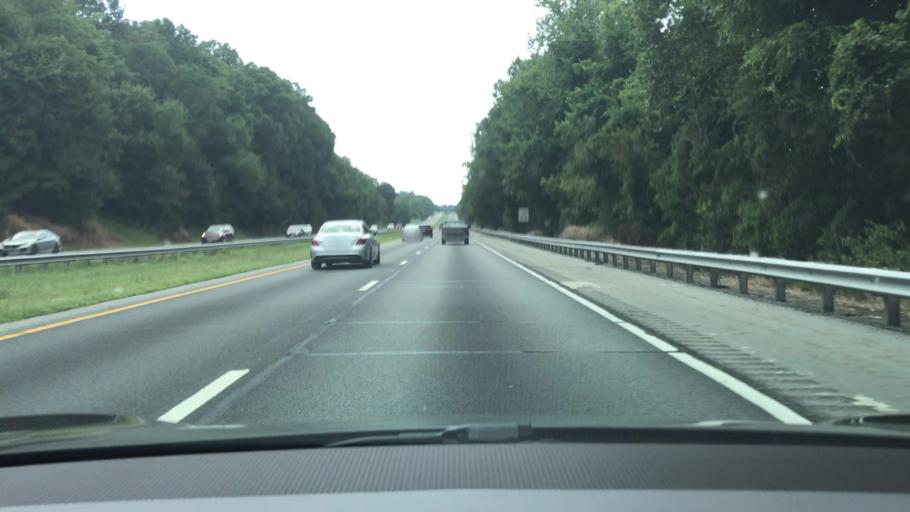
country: US
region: North Carolina
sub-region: Henderson County
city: Mountain Home
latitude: 35.3718
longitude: -82.4718
